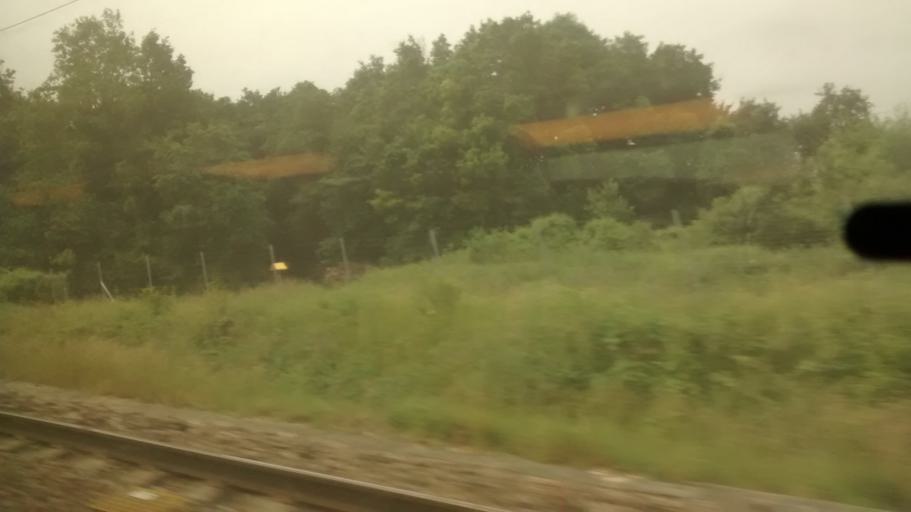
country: FR
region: Ile-de-France
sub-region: Departement de Seine-et-Marne
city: Moisenay
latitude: 48.5648
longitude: 2.7589
